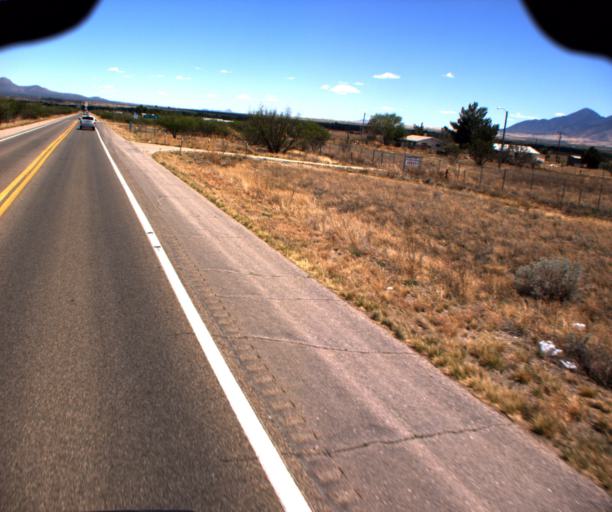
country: US
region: Arizona
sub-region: Cochise County
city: Sierra Vista Southeast
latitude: 31.3799
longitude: -110.1370
